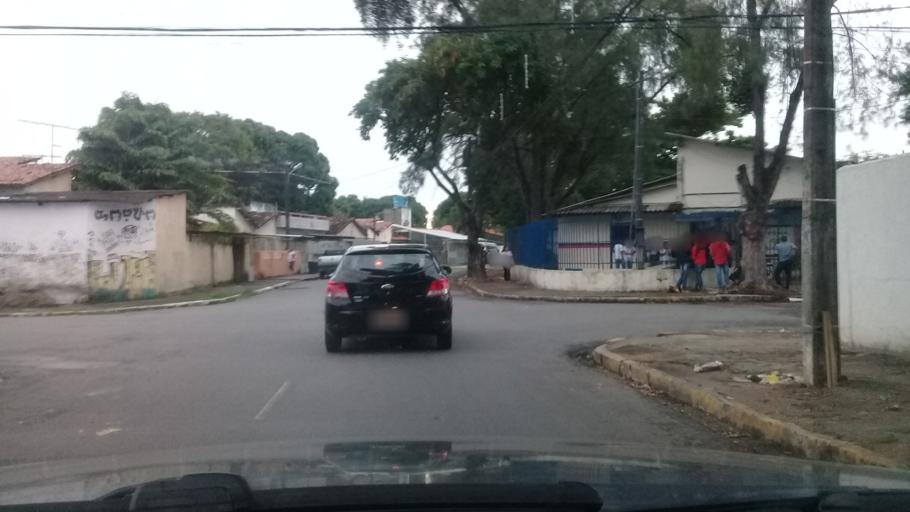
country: BR
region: Pernambuco
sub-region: Recife
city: Recife
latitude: -8.1133
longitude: -34.9245
